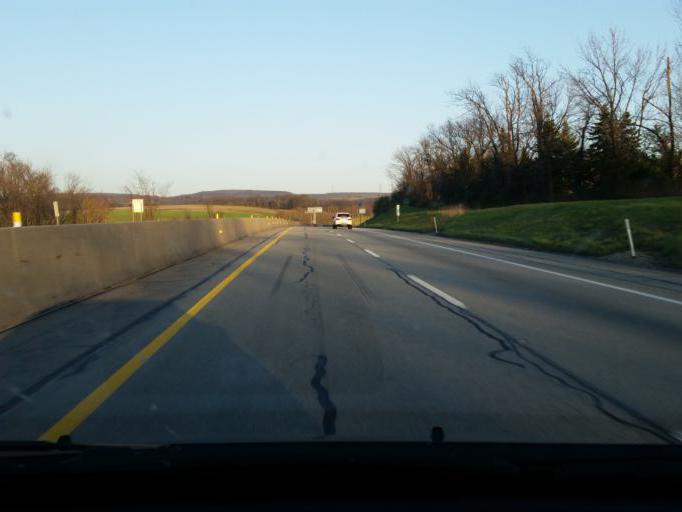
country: US
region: Pennsylvania
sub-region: Westmoreland County
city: Mount Pleasant
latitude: 40.1761
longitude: -79.5109
